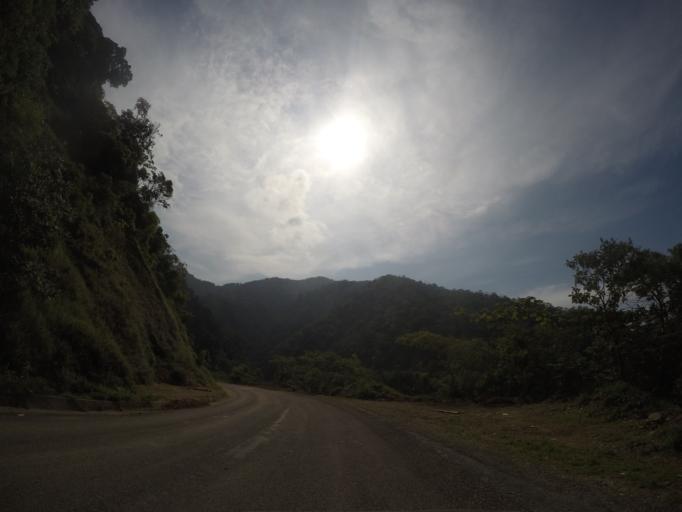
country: MX
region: Oaxaca
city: Pluma Hidalgo
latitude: 15.9383
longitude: -96.4349
